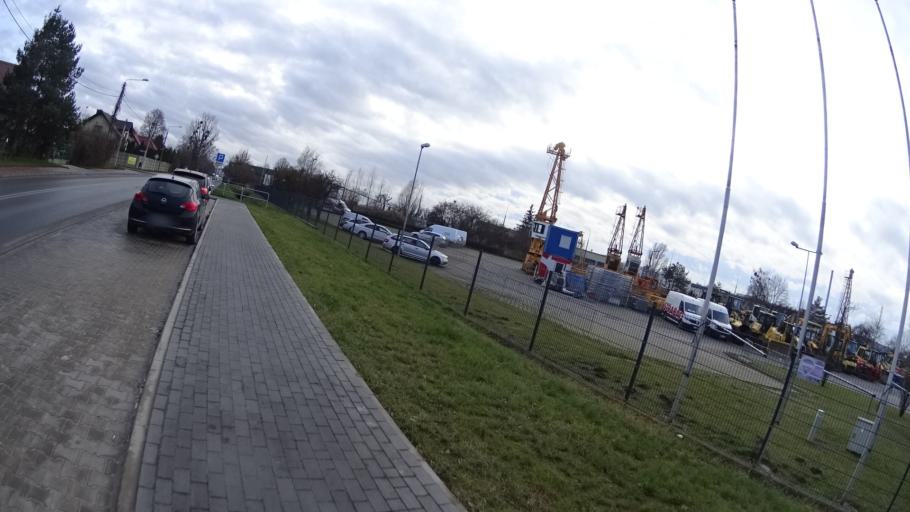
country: PL
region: Masovian Voivodeship
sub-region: Powiat pruszkowski
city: Pruszkow
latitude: 52.1695
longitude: 20.7758
